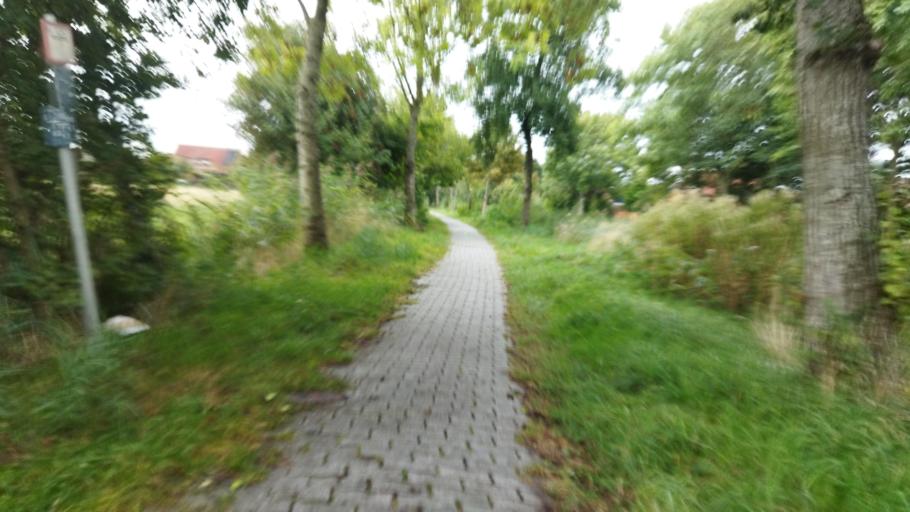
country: DE
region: Lower Saxony
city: Hinte
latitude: 53.4215
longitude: 7.1857
